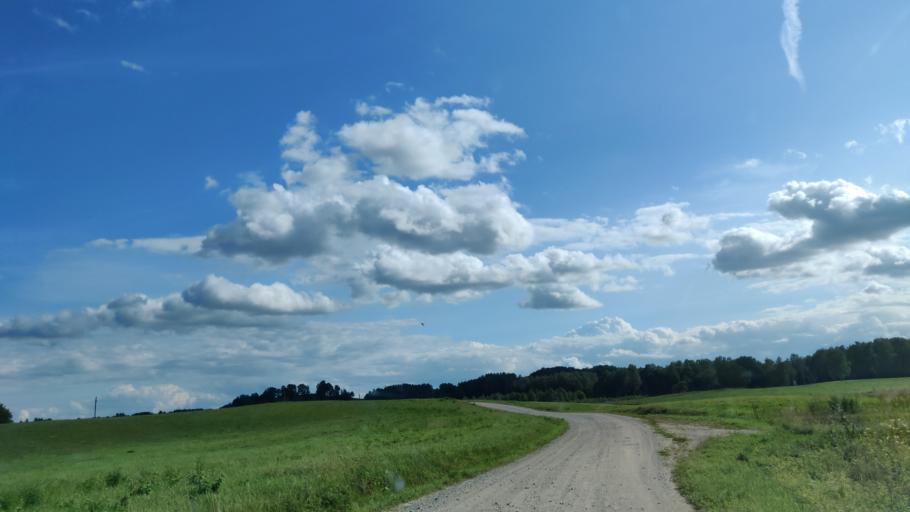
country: LT
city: Varniai
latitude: 55.6060
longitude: 22.3217
